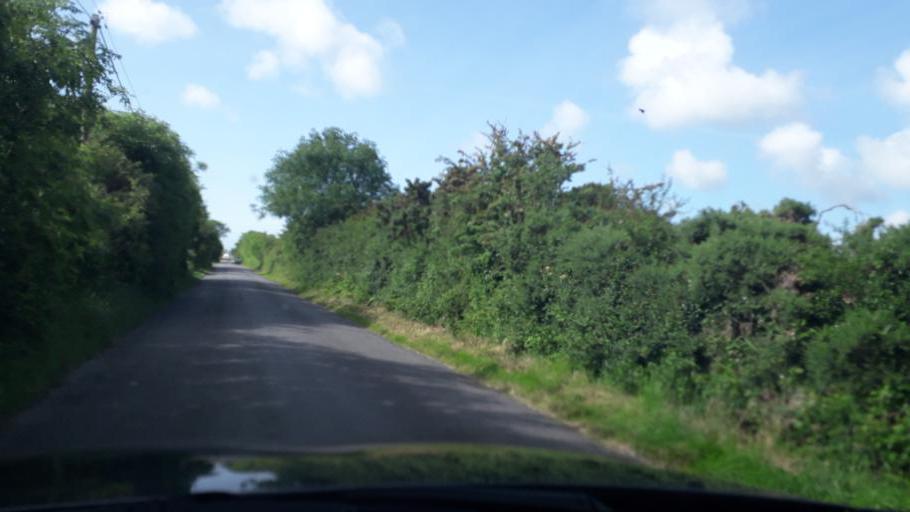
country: IE
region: Leinster
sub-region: Loch Garman
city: Loch Garman
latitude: 52.2491
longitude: -6.5500
